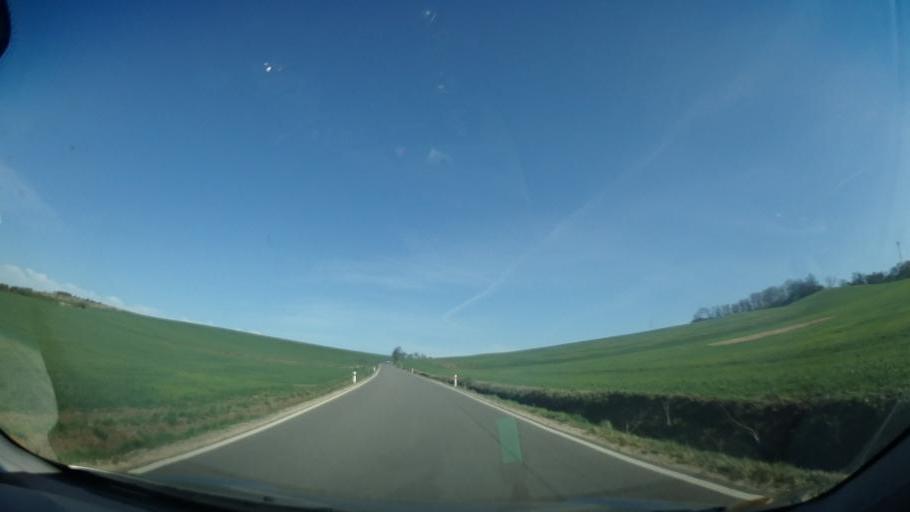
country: CZ
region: South Moravian
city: Ostopovice
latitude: 49.1516
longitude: 16.5598
